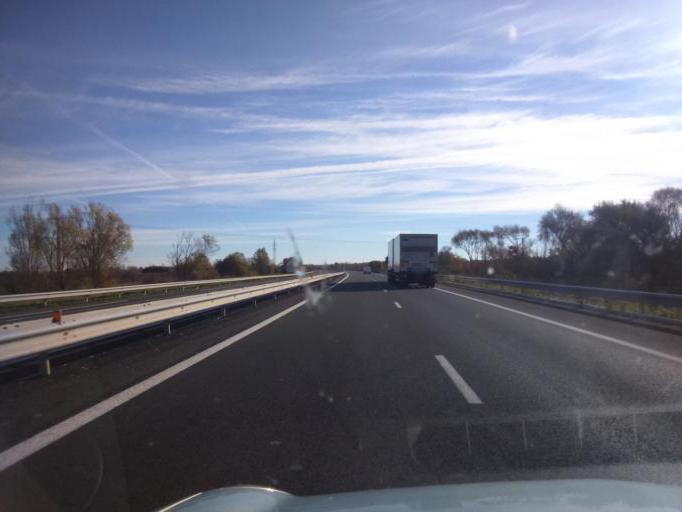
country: FR
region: Poitou-Charentes
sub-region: Departement de la Charente-Maritime
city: Breuil-Magne
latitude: 45.9578
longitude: -0.9386
